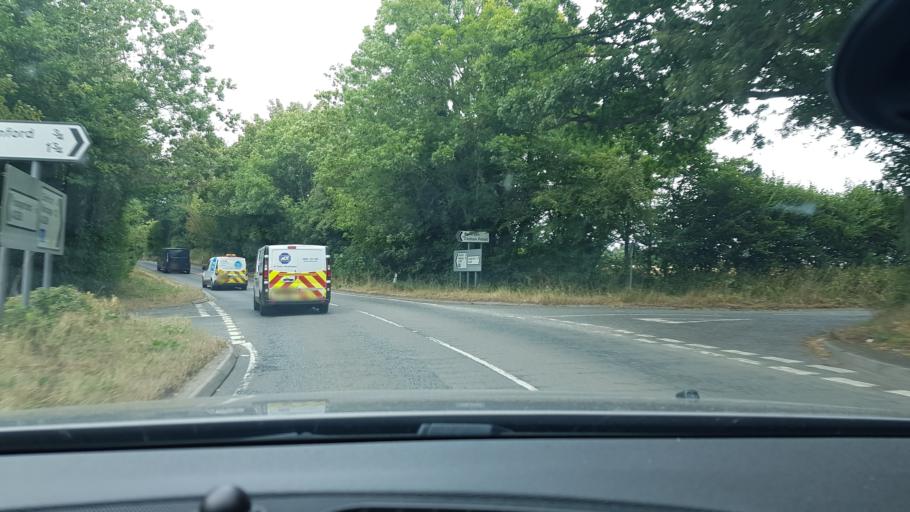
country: GB
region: England
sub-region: West Berkshire
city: Hungerford
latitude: 51.4252
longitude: -1.5011
